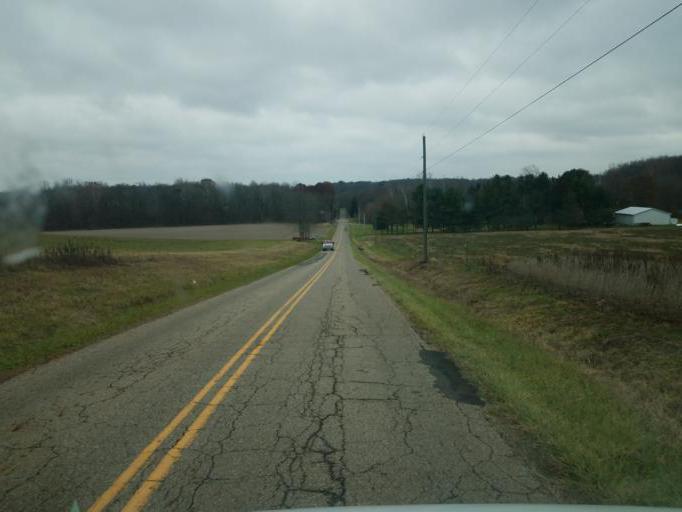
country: US
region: Ohio
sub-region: Knox County
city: Centerburg
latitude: 40.3544
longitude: -82.6257
